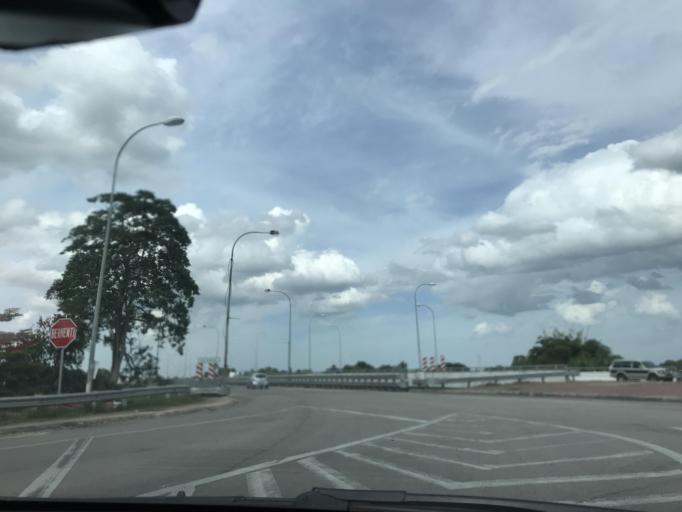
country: MY
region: Kelantan
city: Kampung Lemal
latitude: 6.0301
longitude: 102.1424
